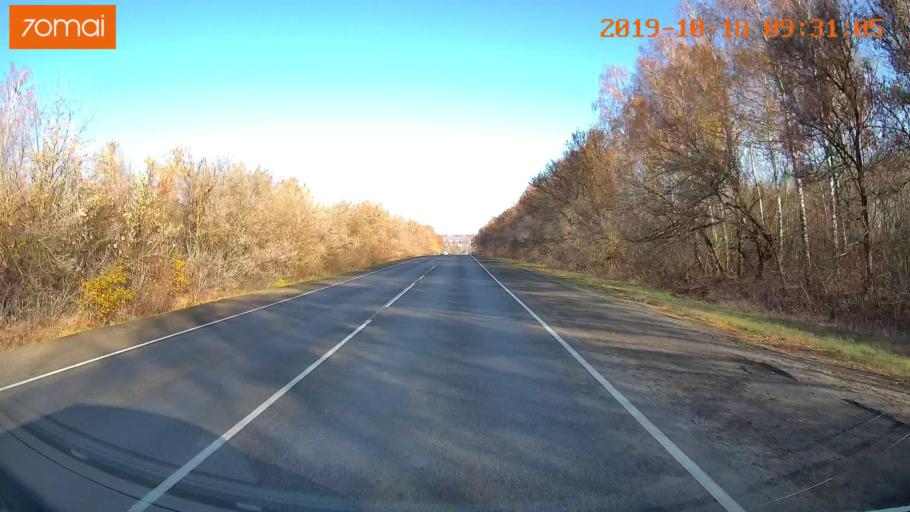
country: RU
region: Tula
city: Yefremov
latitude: 53.1462
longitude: 38.1585
